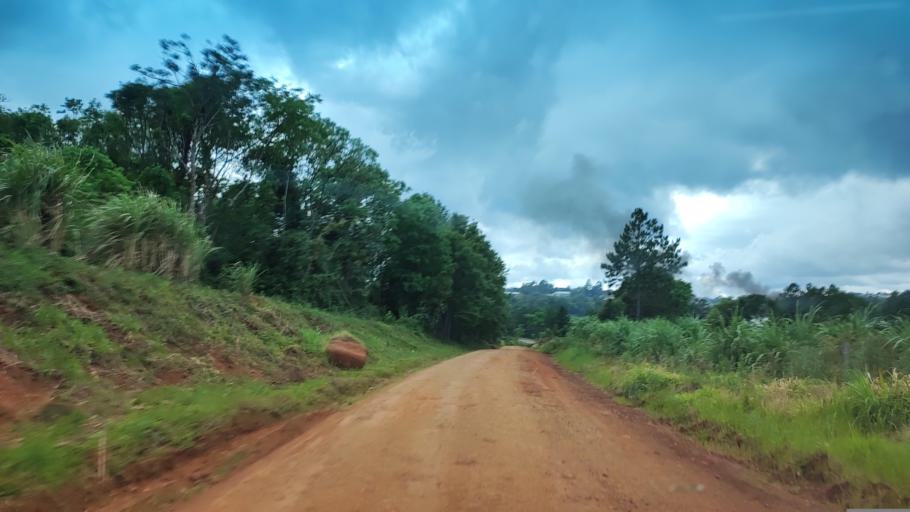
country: AR
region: Misiones
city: Dos de Mayo
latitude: -27.0114
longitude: -54.6191
